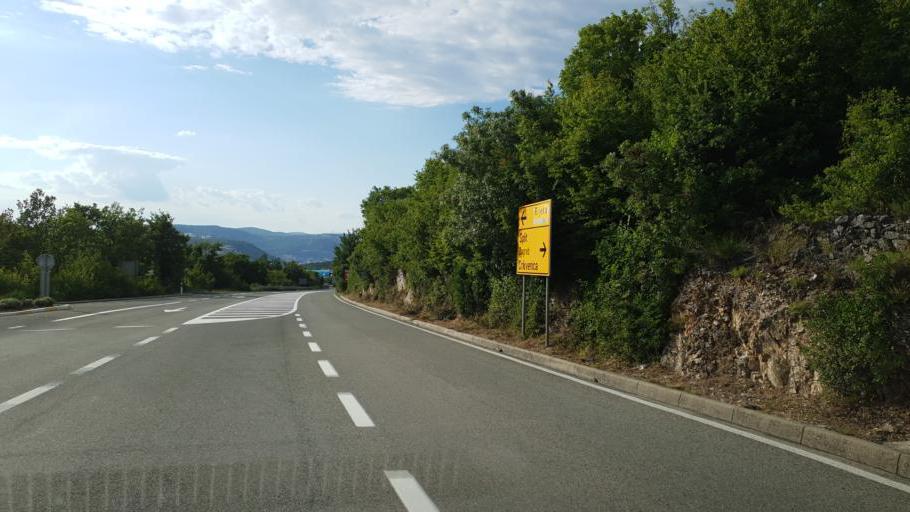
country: HR
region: Primorsko-Goranska
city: Kraljevica
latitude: 45.2699
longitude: 14.5791
